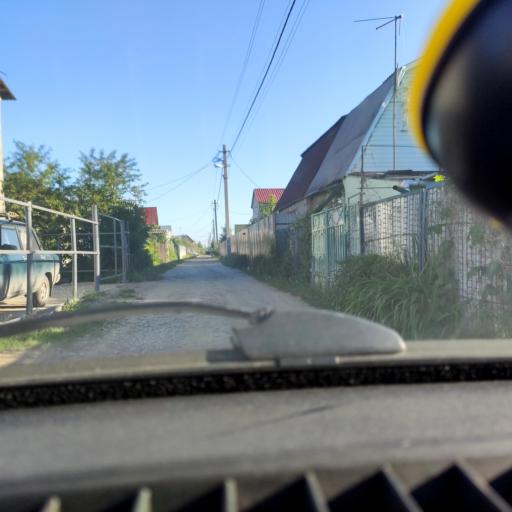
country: RU
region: Samara
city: Tol'yatti
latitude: 53.5937
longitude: 49.3154
